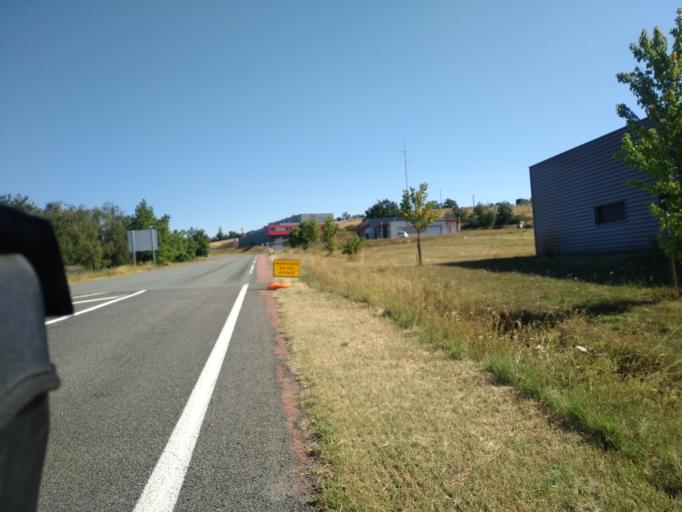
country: FR
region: Rhone-Alpes
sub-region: Departement de la Loire
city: Neulise
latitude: 45.8859
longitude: 4.1789
